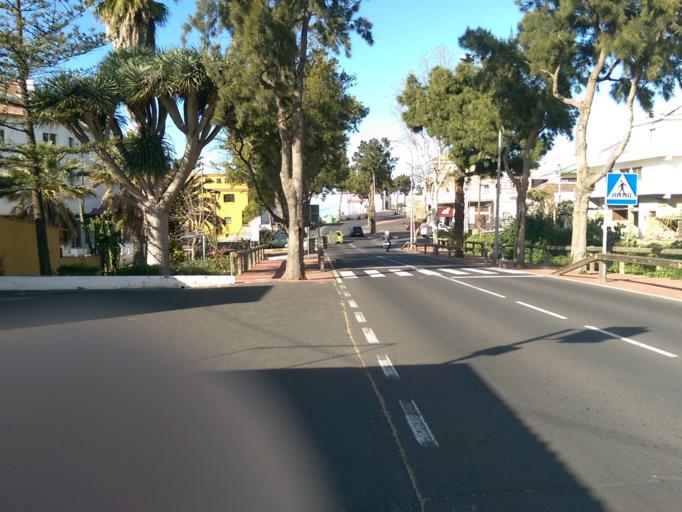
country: ES
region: Canary Islands
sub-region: Provincia de Santa Cruz de Tenerife
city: La Matanza de Acentejo
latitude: 28.4515
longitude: -16.4567
